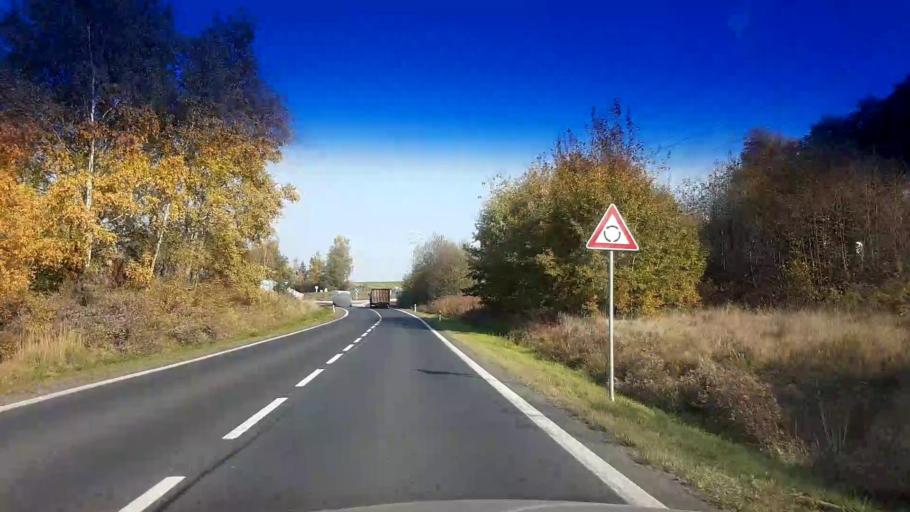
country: CZ
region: Karlovarsky
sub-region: Okres Cheb
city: Cheb
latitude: 50.0743
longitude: 12.3918
